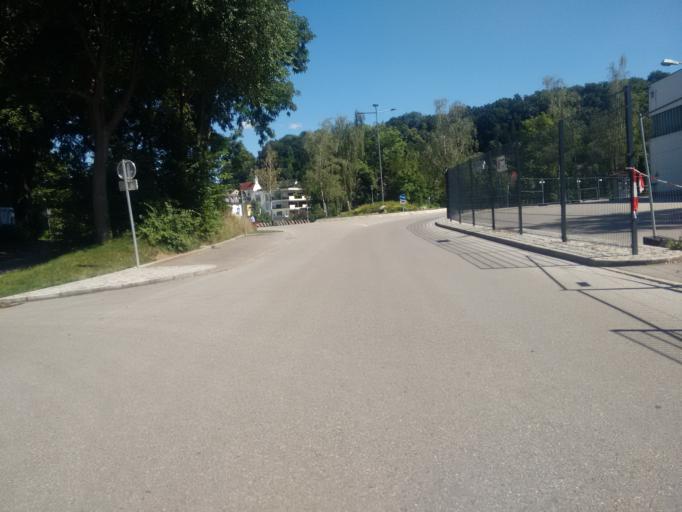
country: AT
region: Upper Austria
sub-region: Wels-Land
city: Thalheim bei Wels
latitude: 48.1536
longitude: 14.0240
